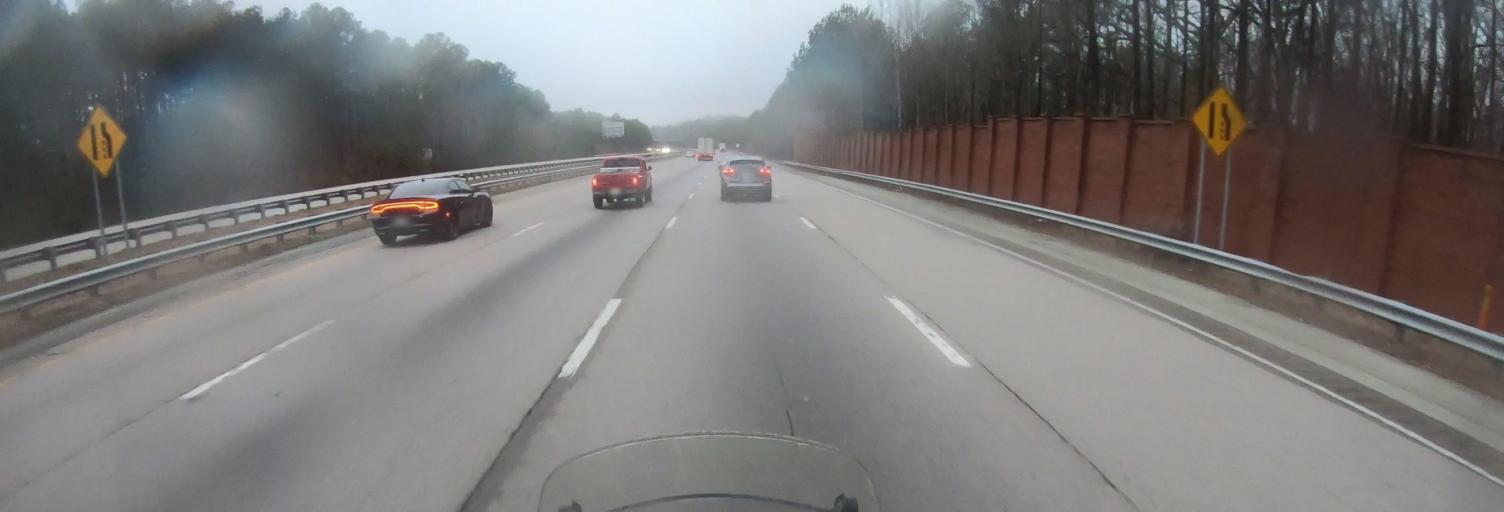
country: US
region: North Carolina
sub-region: Durham County
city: Durham
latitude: 36.0370
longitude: -78.9733
